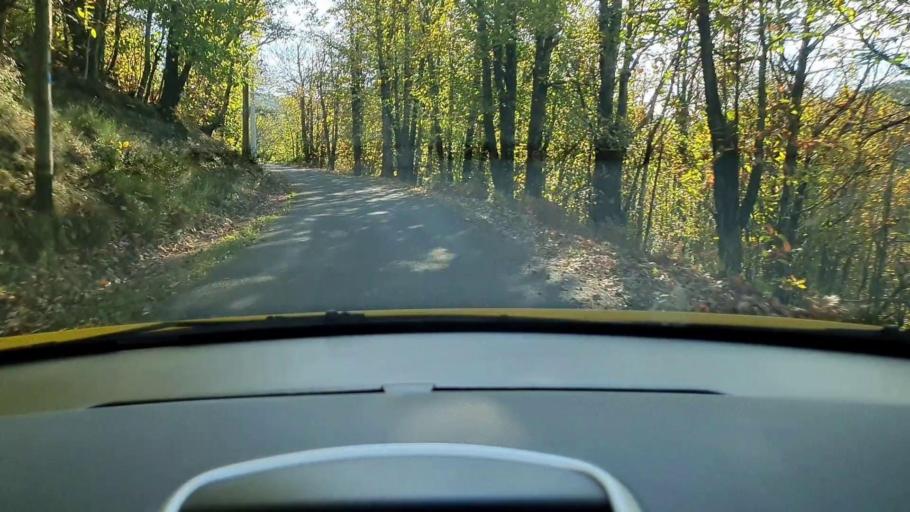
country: FR
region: Languedoc-Roussillon
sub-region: Departement du Gard
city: Sumene
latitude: 44.0133
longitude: 3.7794
